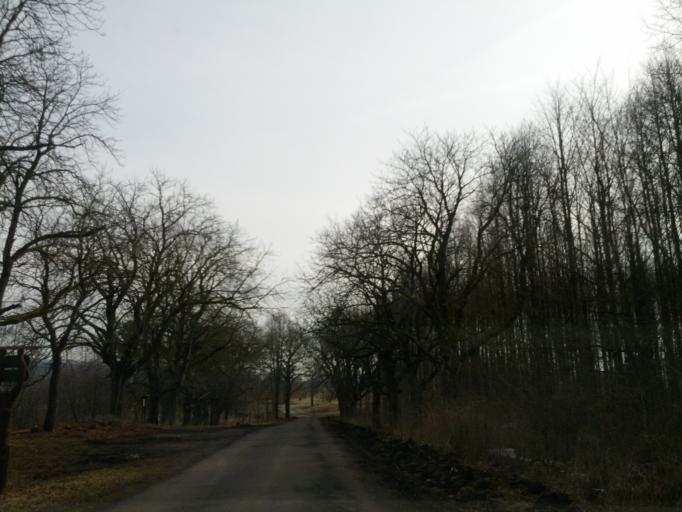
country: DE
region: Thuringia
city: Schweina
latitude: 50.8372
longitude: 10.3267
